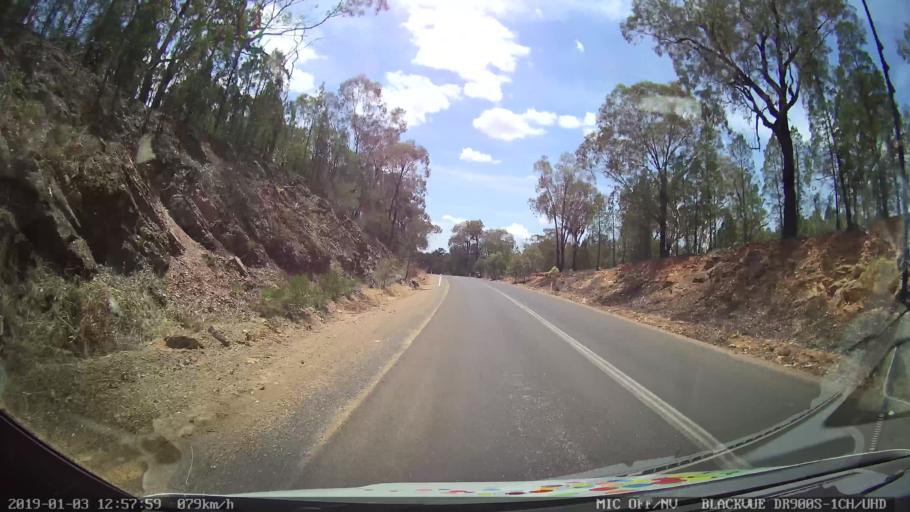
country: AU
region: New South Wales
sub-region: Cabonne
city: Canowindra
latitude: -33.6457
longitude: 148.3694
